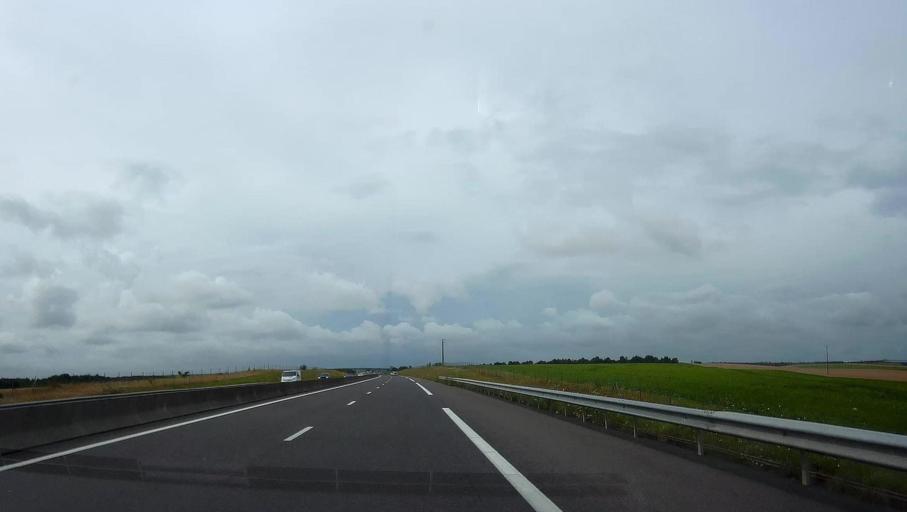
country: FR
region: Champagne-Ardenne
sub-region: Departement de l'Aube
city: Mailly-le-Camp
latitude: 48.7909
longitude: 4.2695
